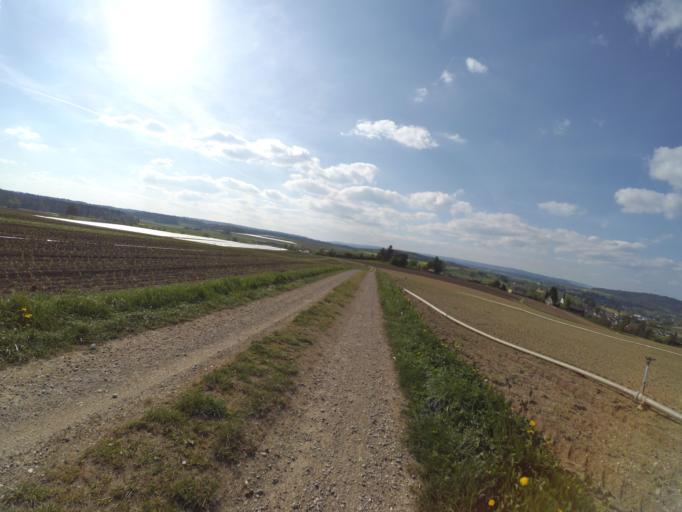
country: CH
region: Thurgau
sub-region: Frauenfeld District
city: Diessenhofen
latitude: 47.6638
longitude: 8.7553
